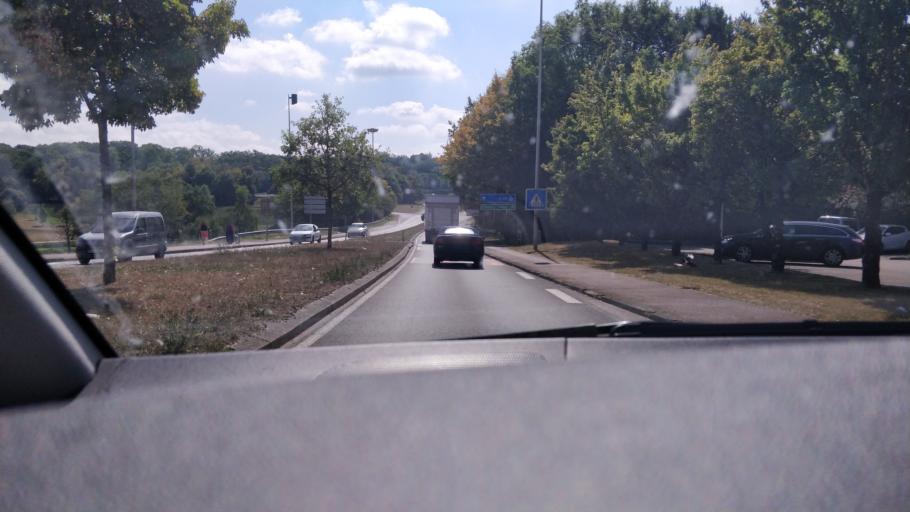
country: FR
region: Limousin
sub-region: Departement de la Haute-Vienne
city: Couzeix
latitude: 45.8660
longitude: 1.2705
